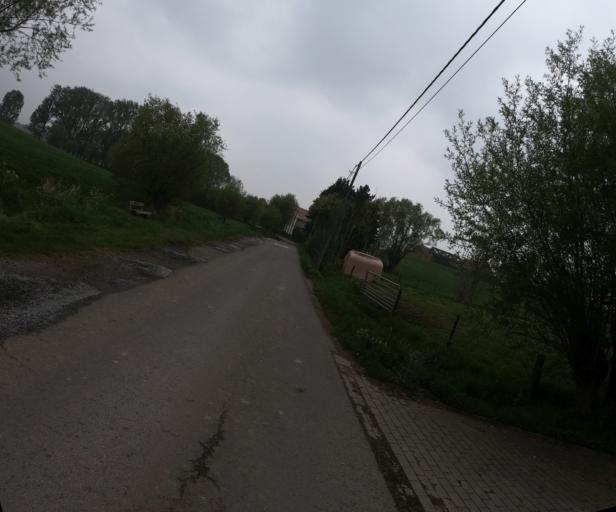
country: BE
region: Flanders
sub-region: Provincie Vlaams-Brabant
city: Halle
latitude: 50.7393
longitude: 4.2020
